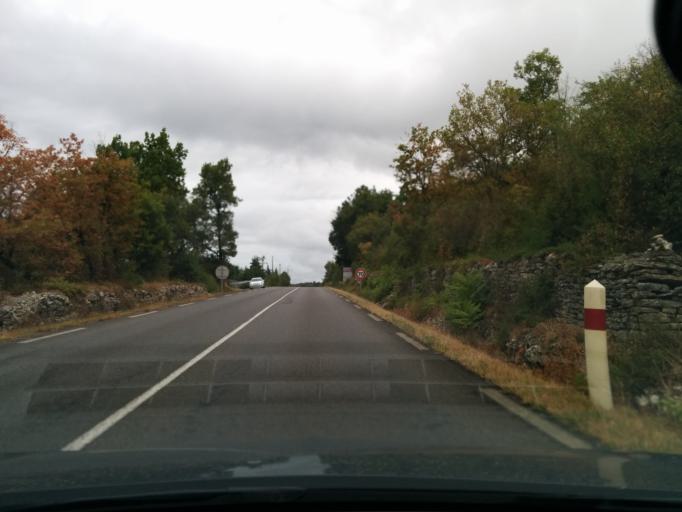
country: FR
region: Limousin
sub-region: Departement de la Correze
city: Brive-la-Gaillarde
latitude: 45.0403
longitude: 1.5013
